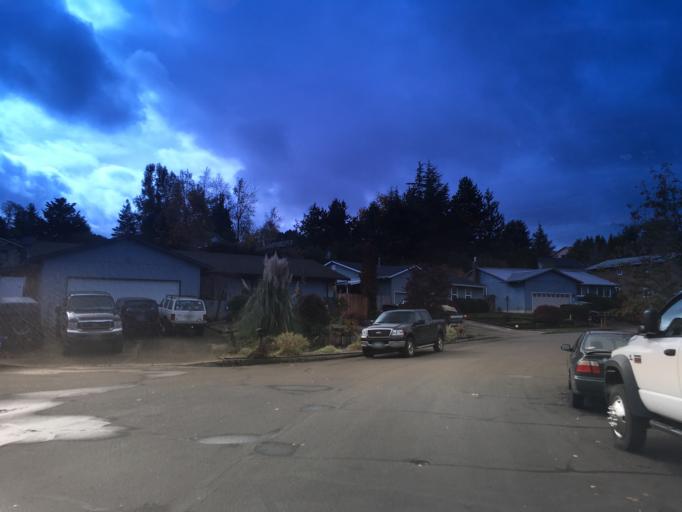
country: US
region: Oregon
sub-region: Multnomah County
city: Fairview
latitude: 45.5369
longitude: -122.4435
